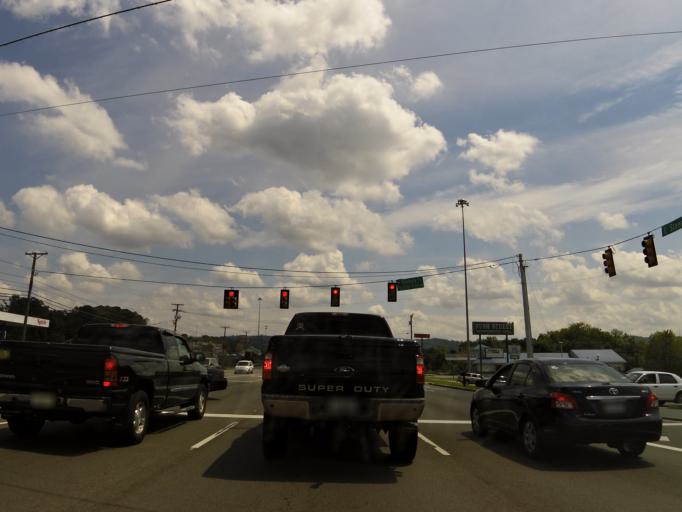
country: US
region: Tennessee
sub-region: Sullivan County
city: Kingsport
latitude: 36.5505
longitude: -82.5262
